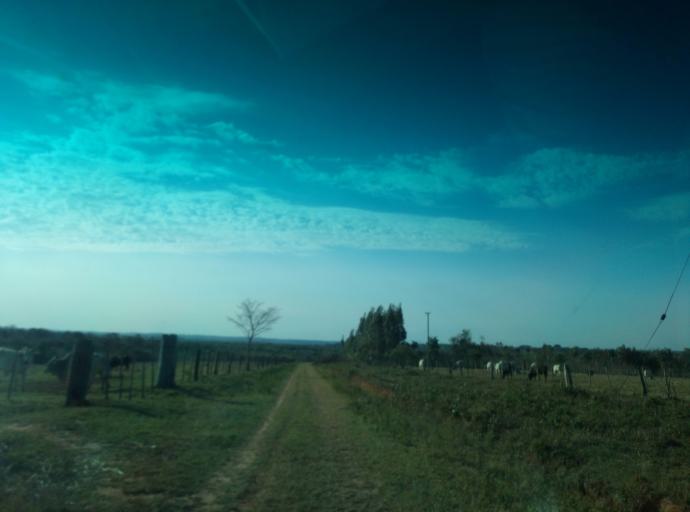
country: PY
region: Caaguazu
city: Doctor Cecilio Baez
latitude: -25.1620
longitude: -56.2321
